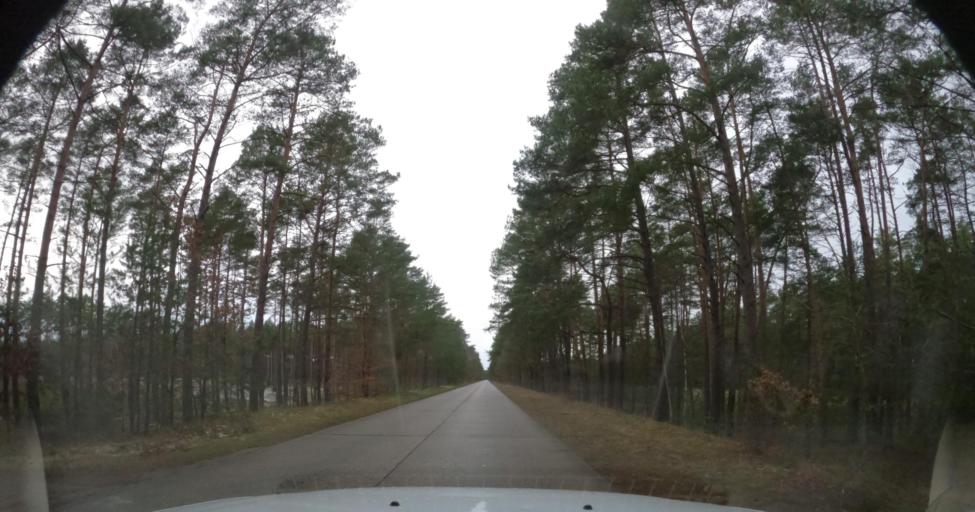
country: PL
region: West Pomeranian Voivodeship
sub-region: Powiat szczecinecki
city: Borne Sulinowo
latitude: 53.5869
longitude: 16.4759
